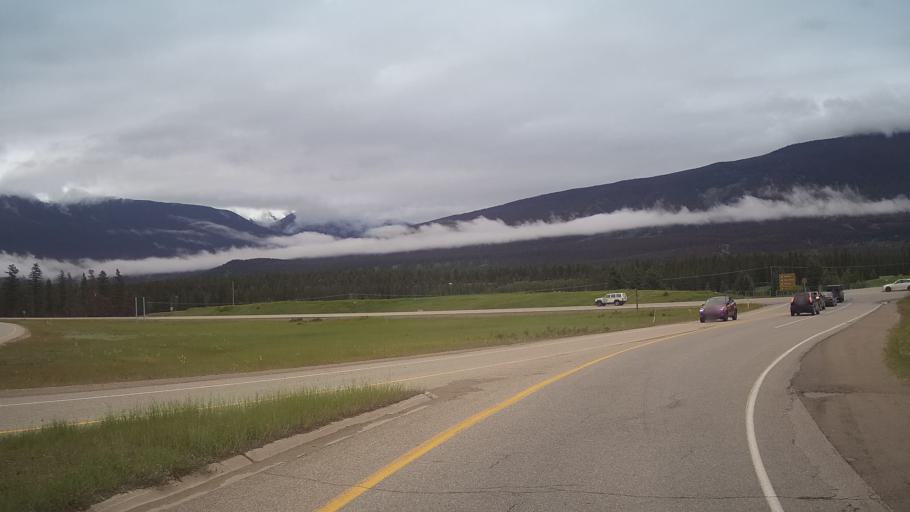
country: CA
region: Alberta
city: Jasper Park Lodge
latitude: 52.8947
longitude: -118.0711
